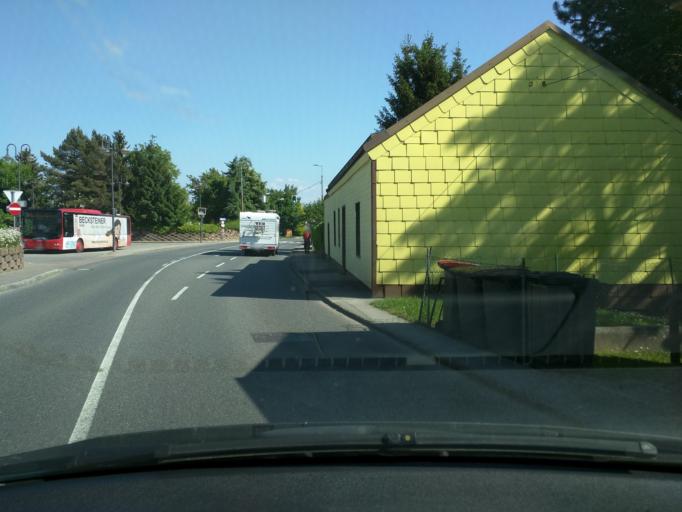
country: AT
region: Lower Austria
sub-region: Politischer Bezirk Melk
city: Ybbs an der Donau
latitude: 48.1766
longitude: 15.0823
